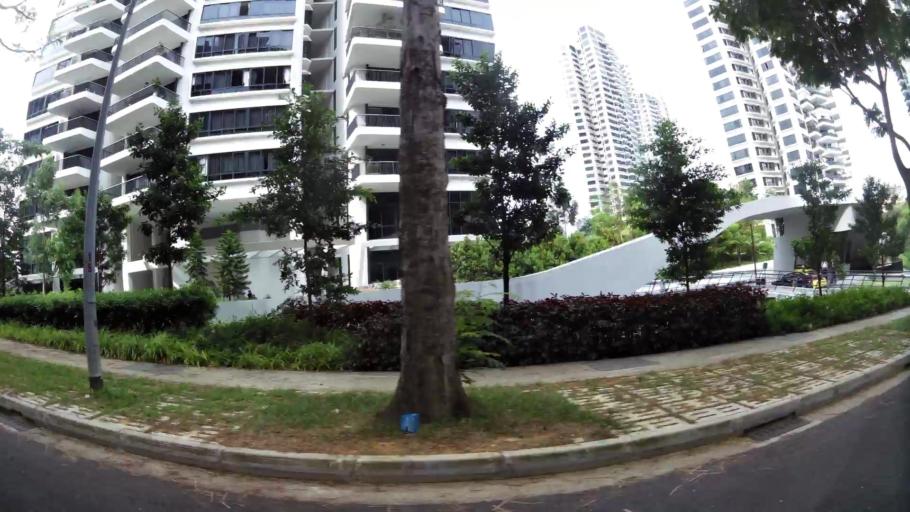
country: SG
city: Singapore
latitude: 1.3146
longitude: 103.8023
